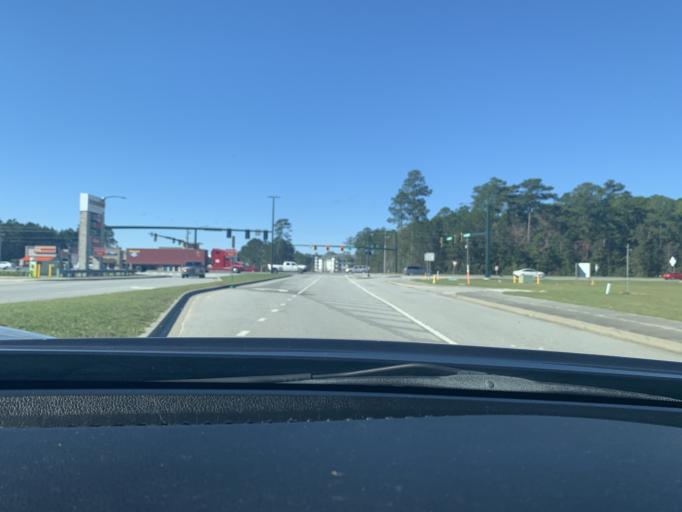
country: US
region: Georgia
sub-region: Chatham County
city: Pooler
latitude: 32.0880
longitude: -81.2763
